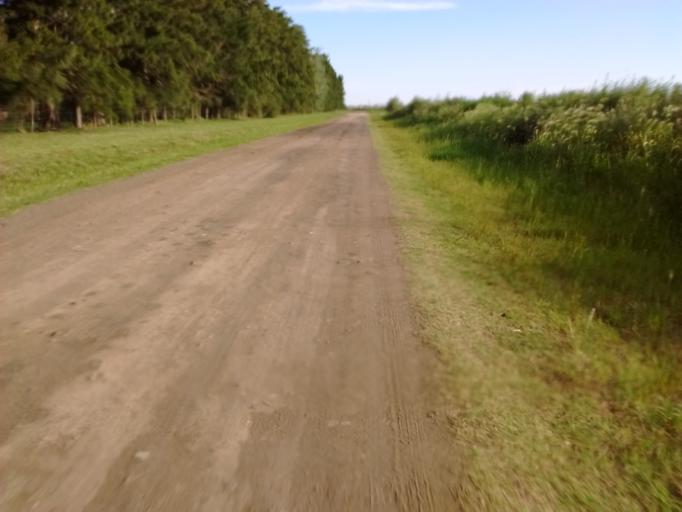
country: AR
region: Santa Fe
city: Funes
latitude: -32.8944
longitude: -60.7974
